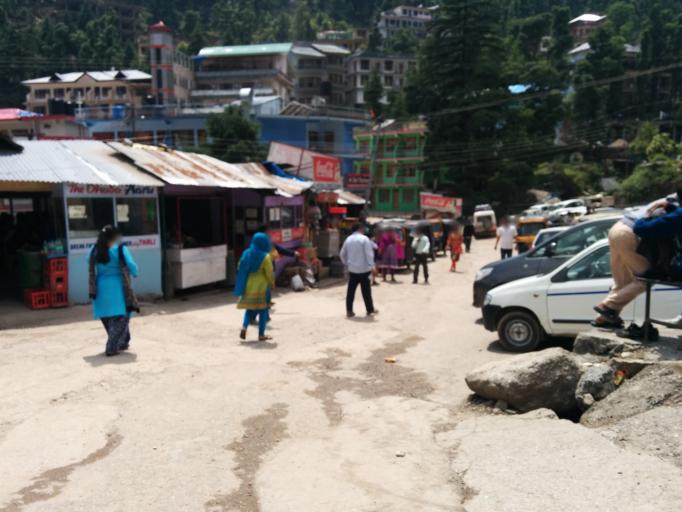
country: IN
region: Himachal Pradesh
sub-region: Kangra
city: Dharmsala
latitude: 32.2435
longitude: 76.3327
